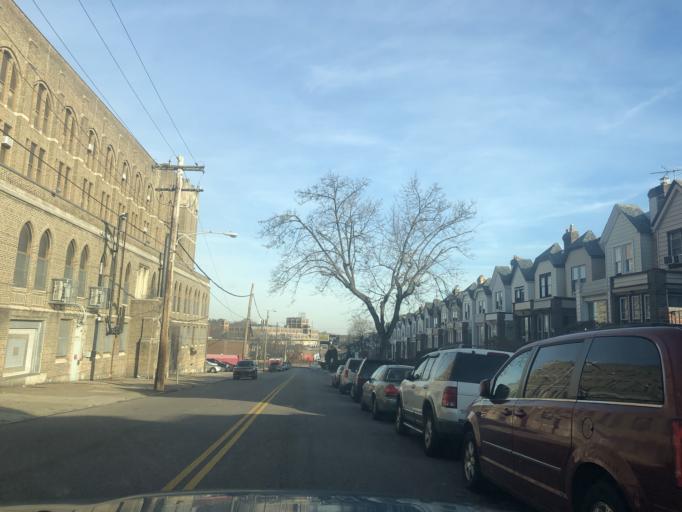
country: US
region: Pennsylvania
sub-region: Delaware County
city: Millbourne
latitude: 39.9804
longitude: -75.2390
